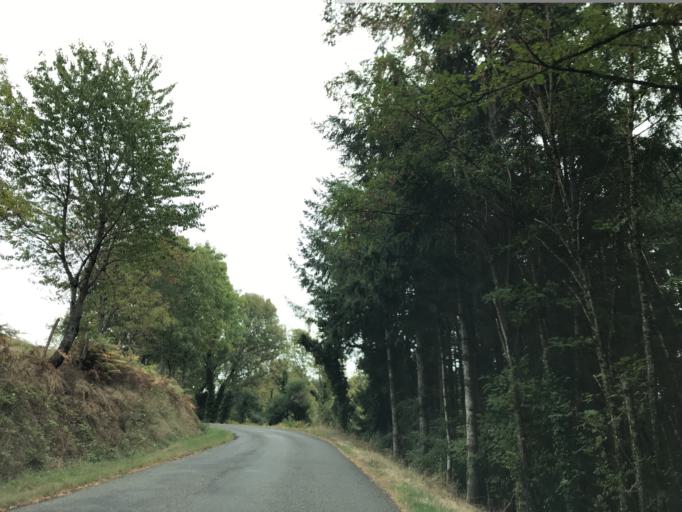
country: FR
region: Auvergne
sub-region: Departement du Puy-de-Dome
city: Thiers
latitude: 45.8380
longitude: 3.5594
